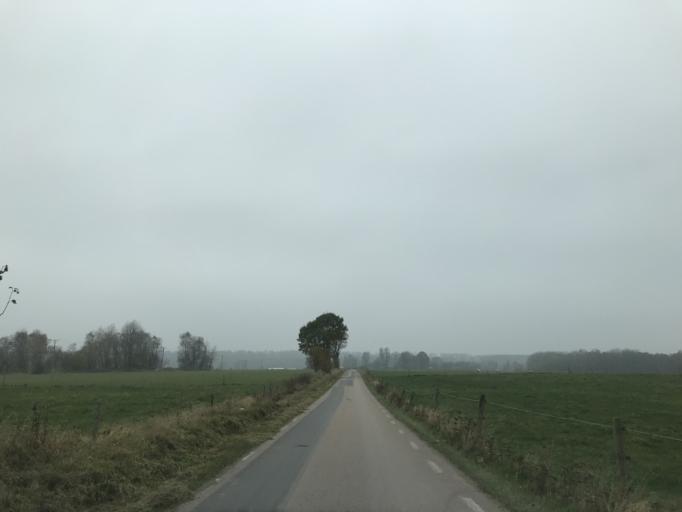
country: SE
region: Skane
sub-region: Klippans Kommun
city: Ljungbyhed
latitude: 55.9957
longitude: 13.2218
